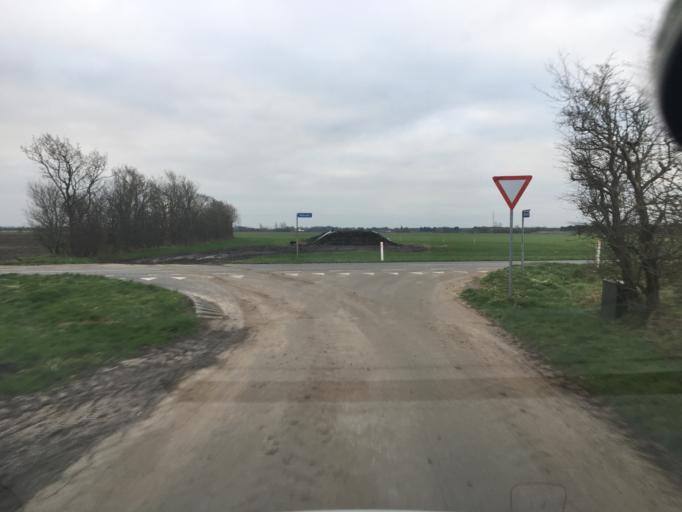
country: DK
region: South Denmark
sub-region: Tonder Kommune
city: Logumkloster
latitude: 55.0474
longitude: 9.0447
